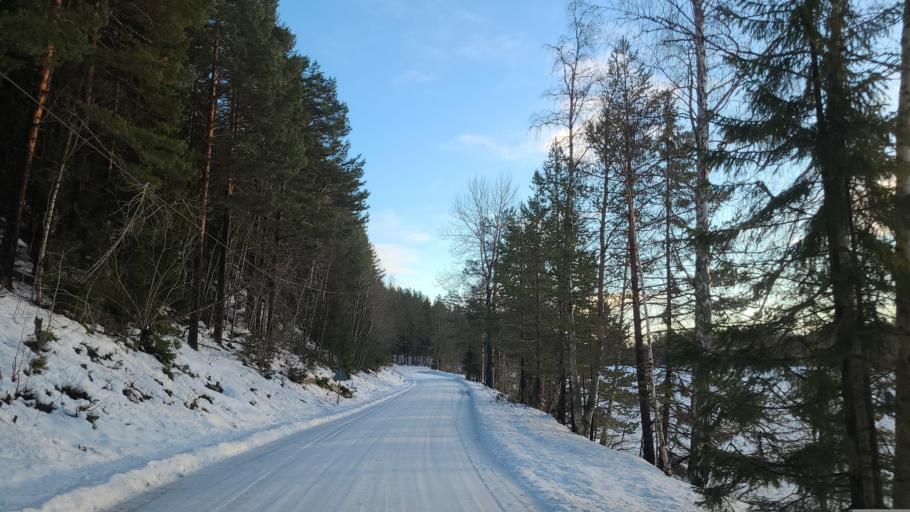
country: SE
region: Gaevleborg
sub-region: Bollnas Kommun
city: Kilafors
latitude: 61.3891
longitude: 16.6859
